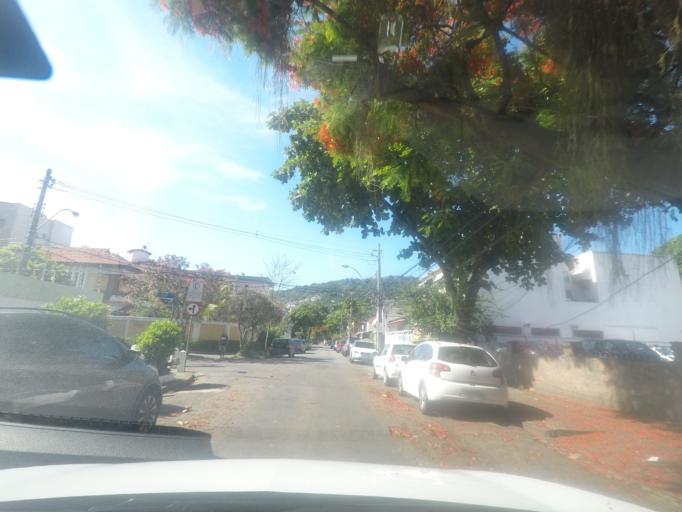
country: BR
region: Rio de Janeiro
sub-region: Niteroi
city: Niteroi
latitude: -22.9199
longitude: -43.0926
